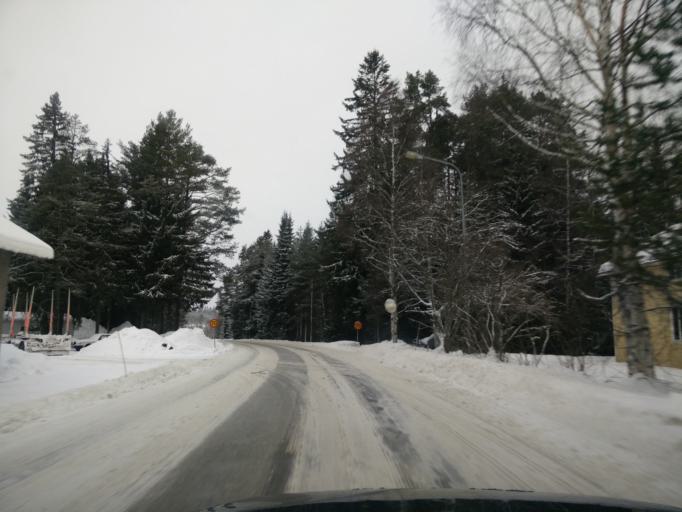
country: SE
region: Jaemtland
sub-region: Braecke Kommun
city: Braecke
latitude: 62.3978
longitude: 15.2086
